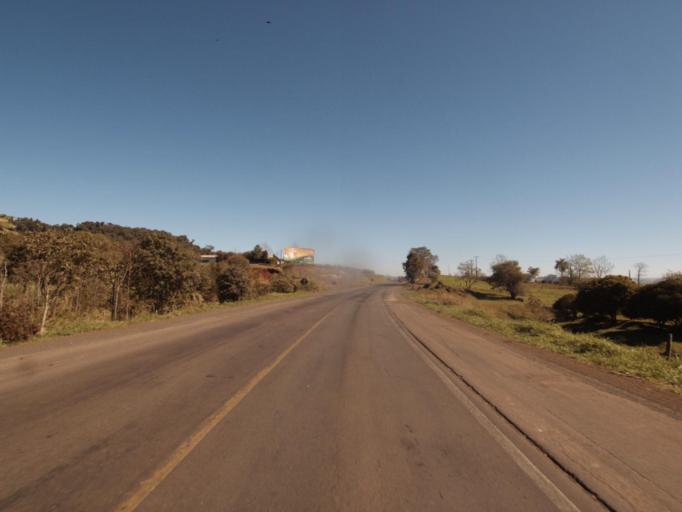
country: BR
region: Rio Grande do Sul
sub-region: Frederico Westphalen
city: Frederico Westphalen
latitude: -26.8014
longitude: -53.3541
